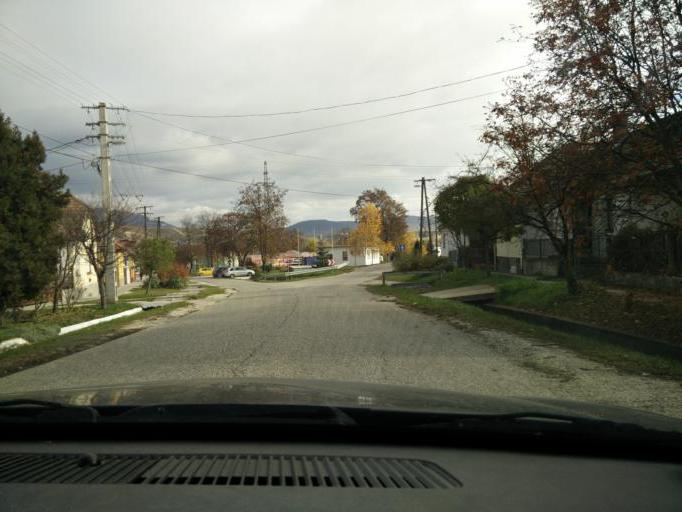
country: HU
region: Komarom-Esztergom
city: Kesztolc
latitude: 47.6786
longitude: 18.7752
